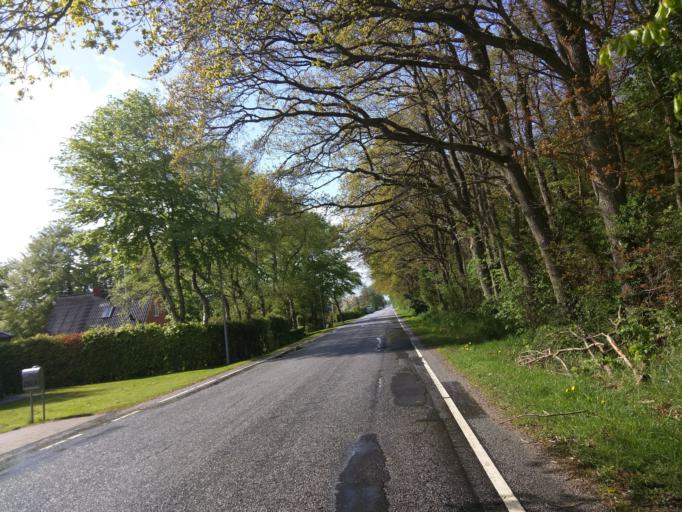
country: DK
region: Central Jutland
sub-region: Viborg Kommune
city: Viborg
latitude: 56.4119
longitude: 9.4180
